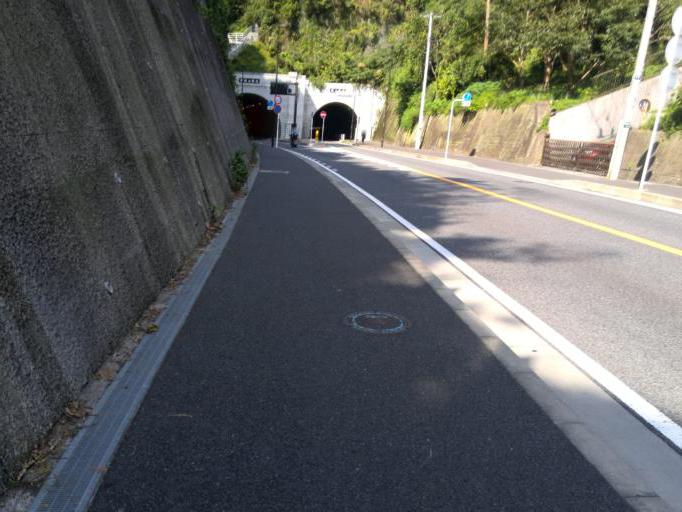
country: JP
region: Kanagawa
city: Zushi
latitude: 35.2852
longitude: 139.5801
